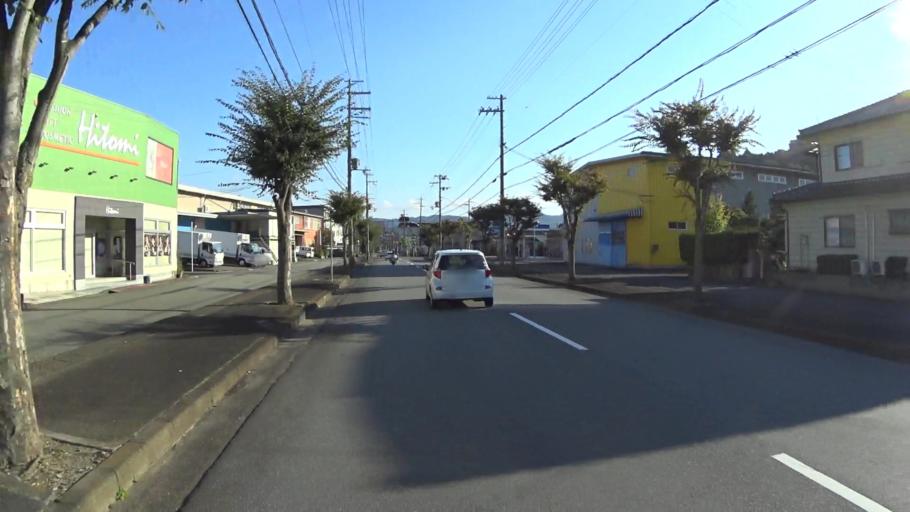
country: JP
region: Kyoto
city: Fukuchiyama
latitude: 35.3088
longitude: 135.1094
